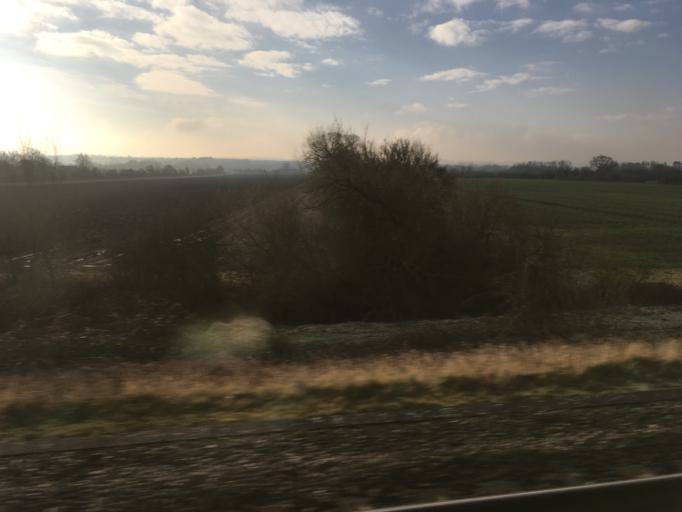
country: GB
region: England
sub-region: Oxfordshire
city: Grove
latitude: 51.6205
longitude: -1.3934
